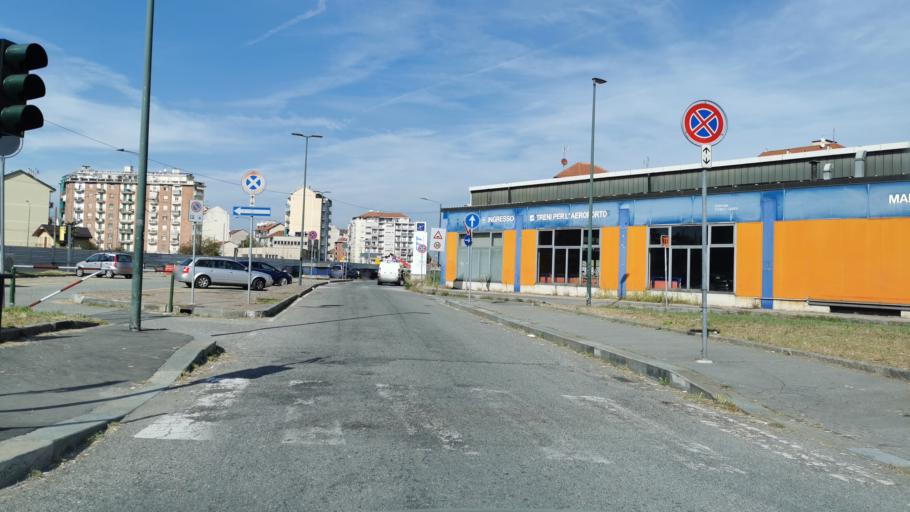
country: IT
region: Piedmont
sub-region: Provincia di Torino
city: Venaria Reale
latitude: 45.1035
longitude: 7.6633
